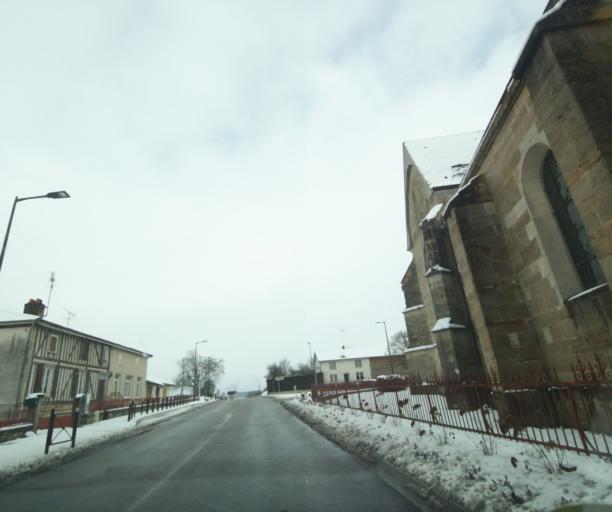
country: FR
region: Champagne-Ardenne
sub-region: Departement de la Haute-Marne
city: Montier-en-Der
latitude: 48.4344
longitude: 4.7251
